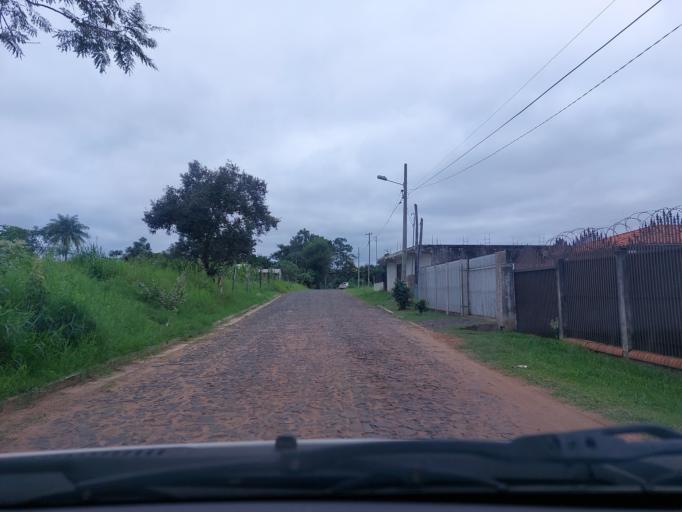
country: PY
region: San Pedro
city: Guayaybi
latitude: -24.6675
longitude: -56.4330
